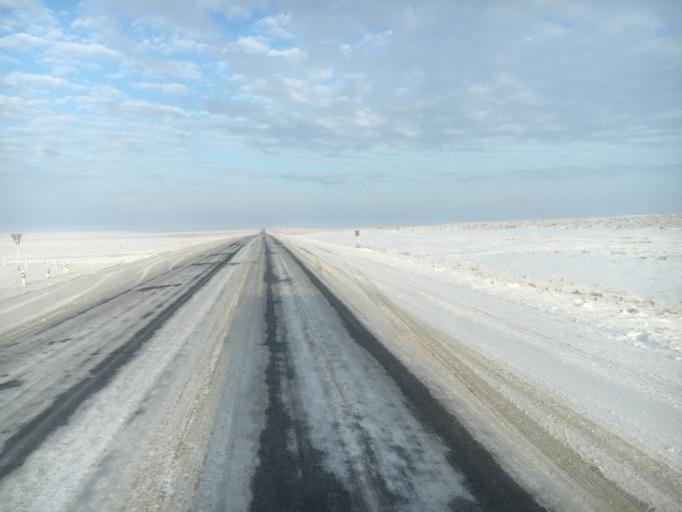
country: KZ
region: Qyzylorda
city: Sekseuil
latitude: 47.7168
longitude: 61.3965
